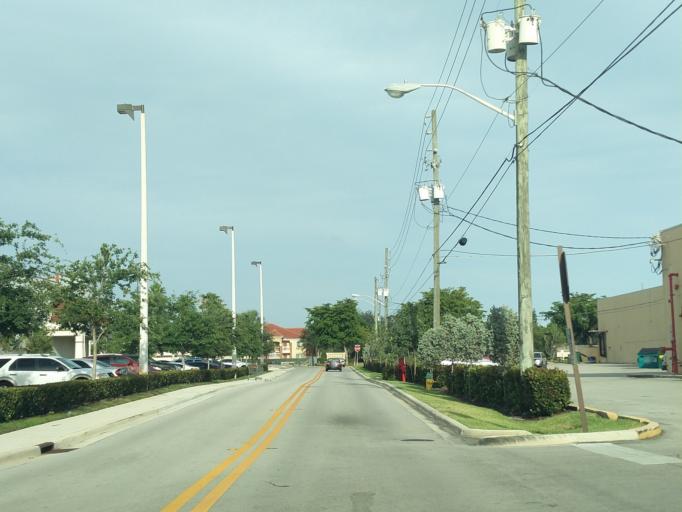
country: US
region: Florida
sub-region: Broward County
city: Pine Island Ridge
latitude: 26.0960
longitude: -80.2483
